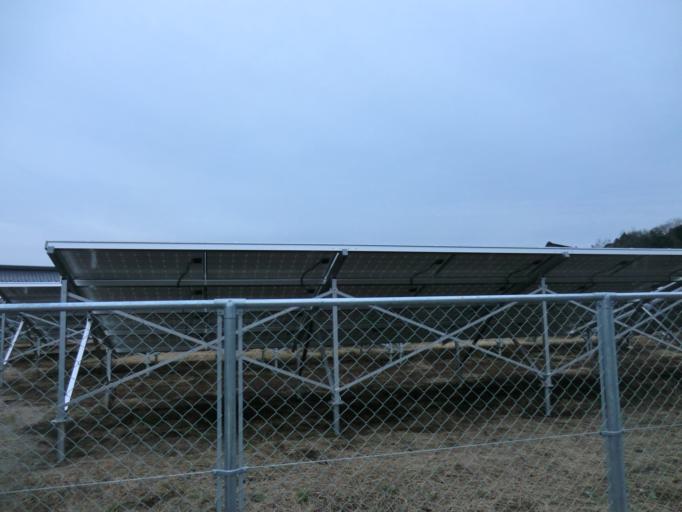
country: JP
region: Ibaraki
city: Naka
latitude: 36.0976
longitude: 140.1147
